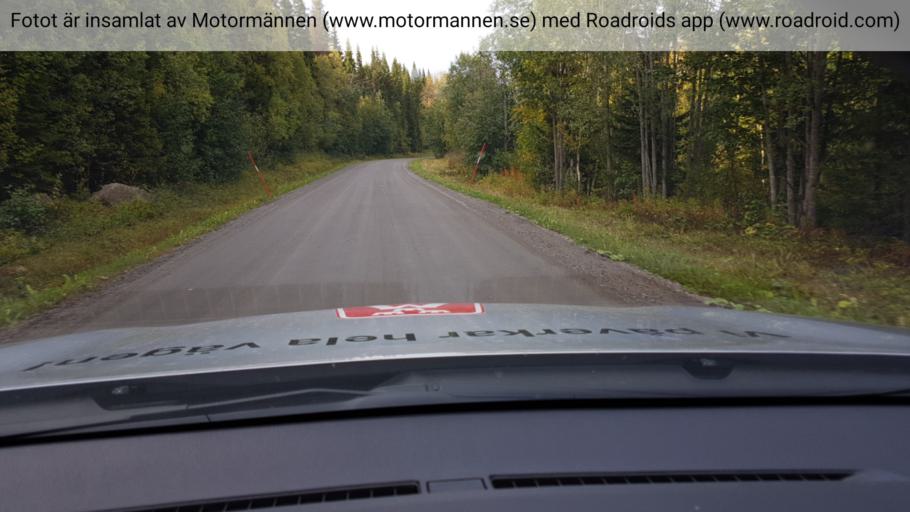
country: SE
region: Jaemtland
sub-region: Stroemsunds Kommun
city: Stroemsund
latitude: 64.0028
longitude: 15.8163
